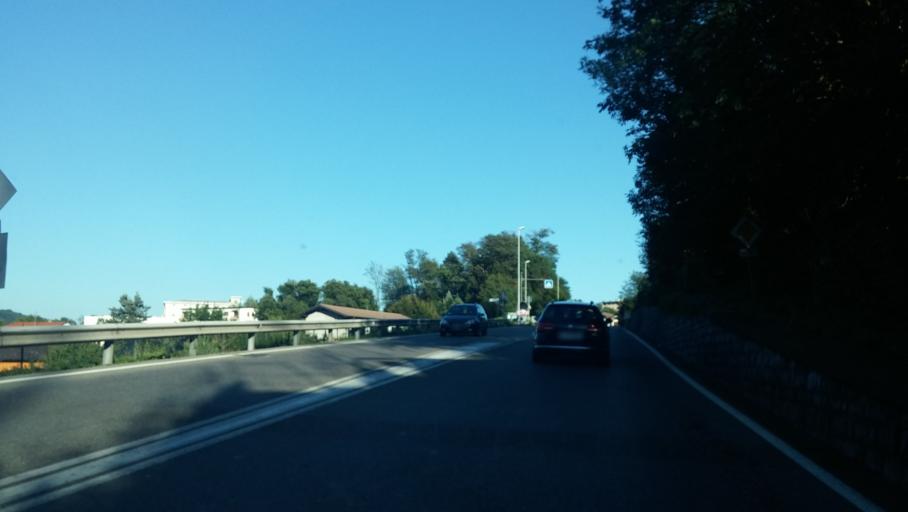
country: IT
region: Lombardy
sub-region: Provincia di Como
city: Tavernerio
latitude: 45.7959
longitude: 9.1315
